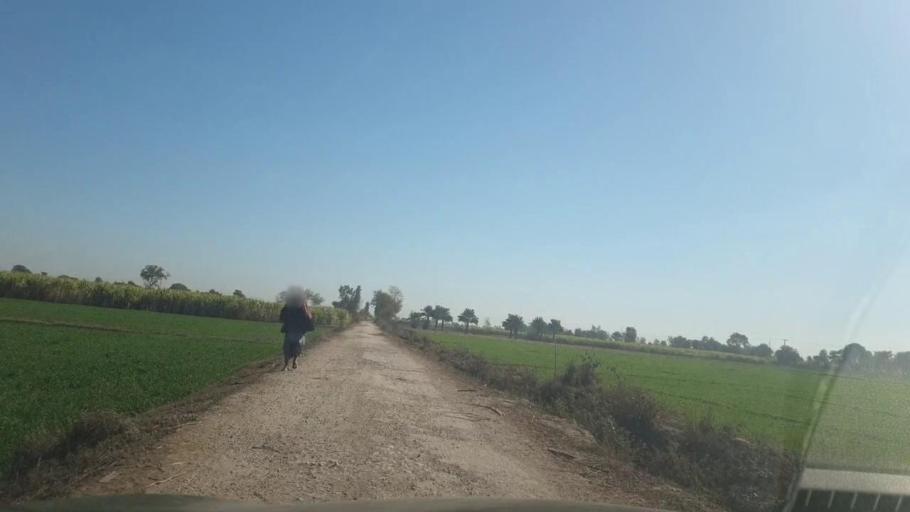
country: PK
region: Sindh
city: Ghotki
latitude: 27.9746
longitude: 69.3343
